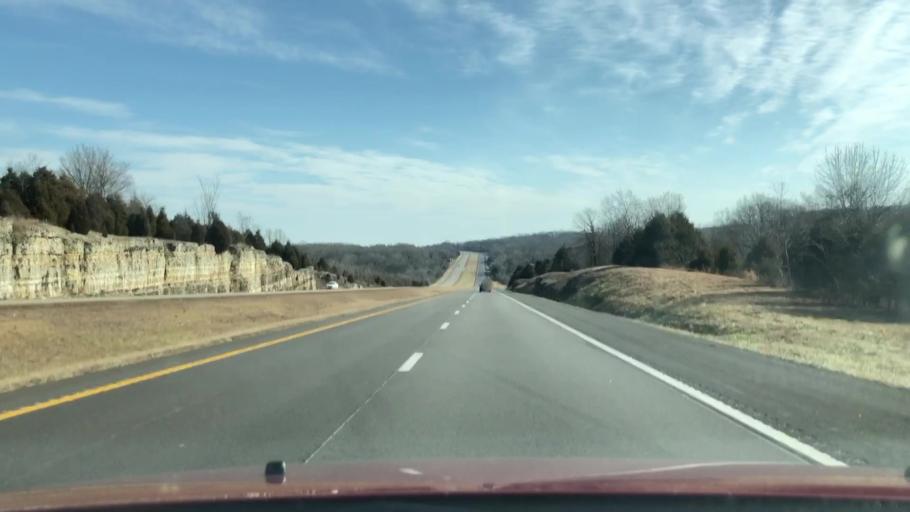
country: US
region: Missouri
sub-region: Wright County
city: Mansfield
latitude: 37.1123
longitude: -92.6619
